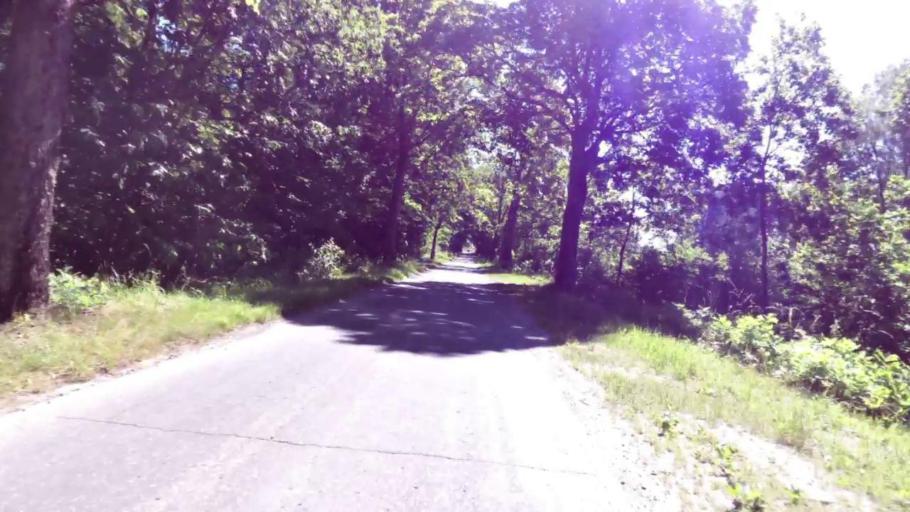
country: PL
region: West Pomeranian Voivodeship
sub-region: Powiat bialogardzki
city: Bialogard
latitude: 53.9397
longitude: 15.9768
